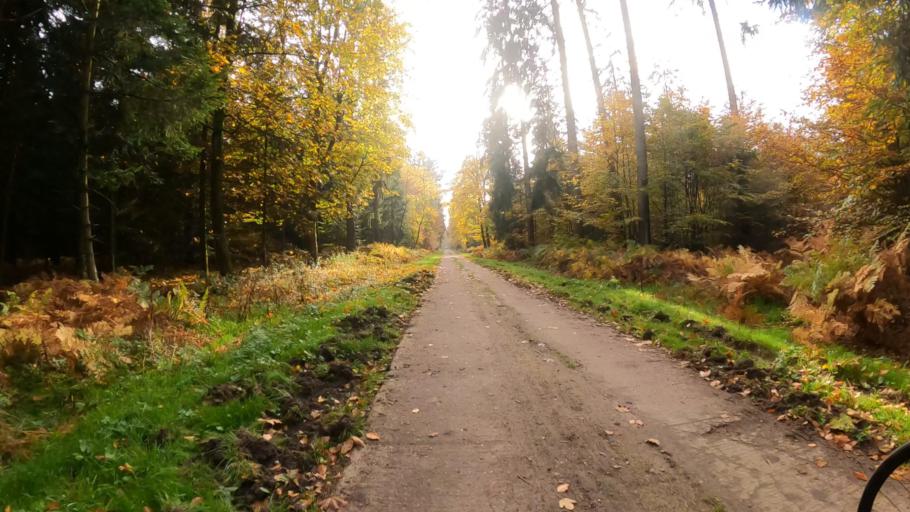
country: DE
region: Lower Saxony
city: Buchholz in der Nordheide
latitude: 53.3573
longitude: 9.8225
